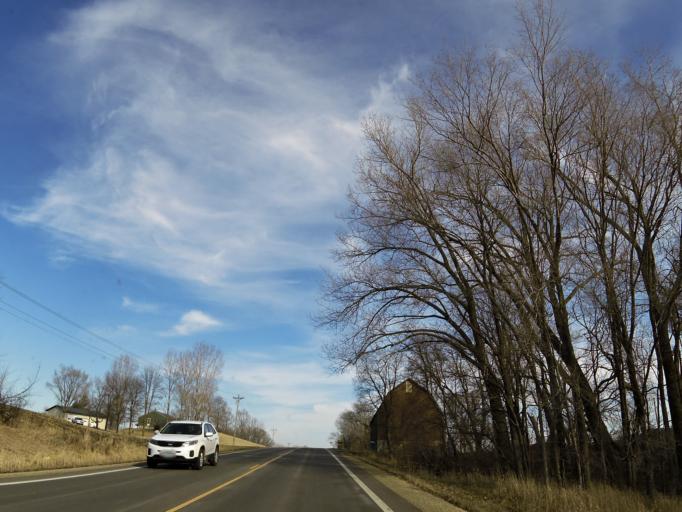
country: US
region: Minnesota
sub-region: Scott County
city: Elko New Market
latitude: 44.5439
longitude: -93.3705
